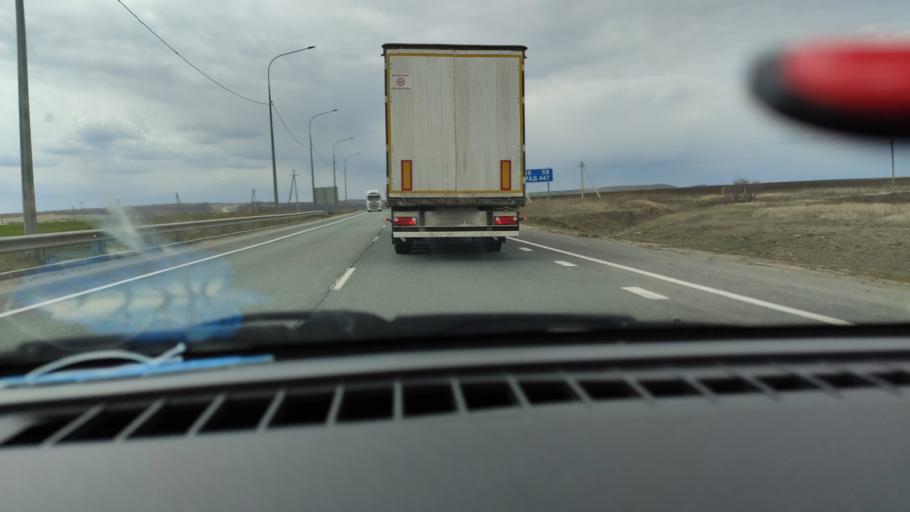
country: RU
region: Saratov
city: Yelshanka
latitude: 51.8300
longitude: 46.4069
